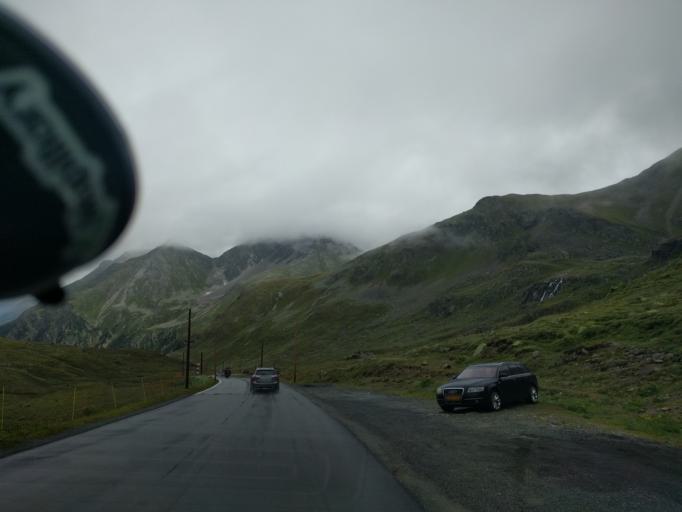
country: CH
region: Grisons
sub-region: Praettigau/Davos District
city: Davos
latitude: 46.7442
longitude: 9.9619
